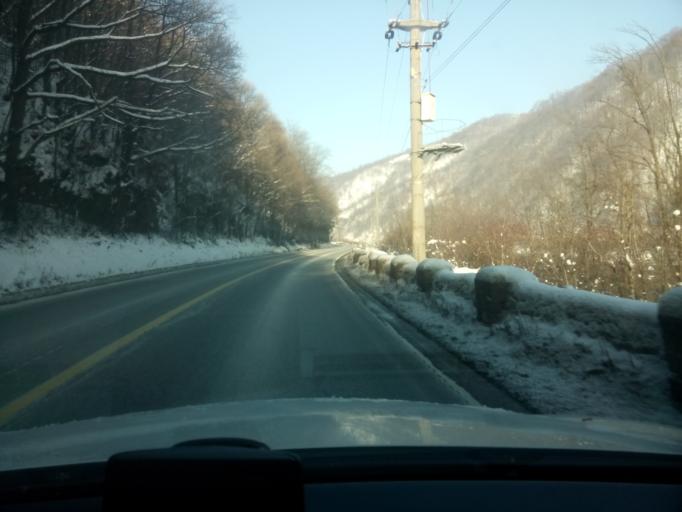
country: RO
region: Sibiu
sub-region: Comuna Boita
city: Boita
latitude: 45.5947
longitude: 24.2606
